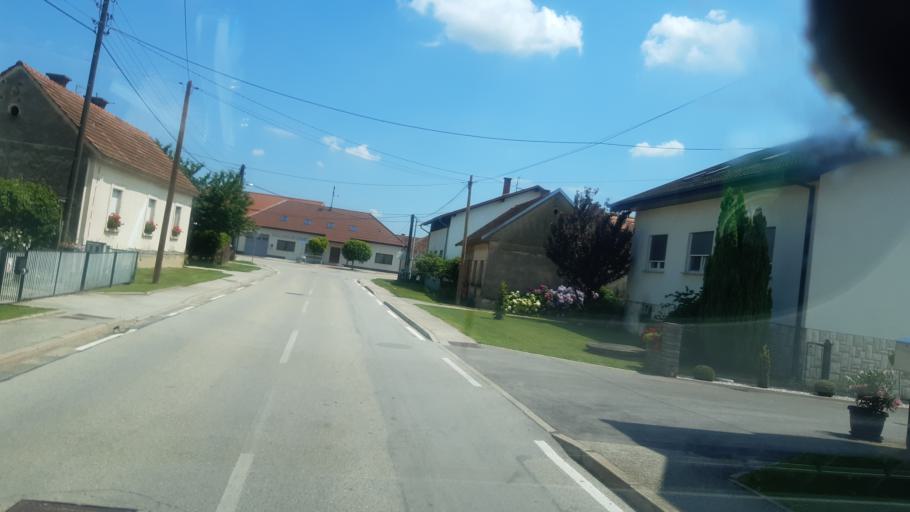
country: SI
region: Moravske Toplice
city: Moravske Toplice
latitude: 46.6681
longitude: 16.2257
